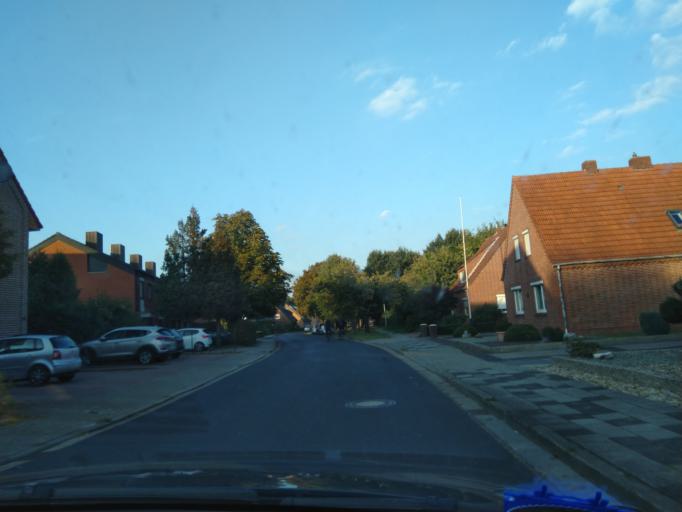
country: DE
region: Lower Saxony
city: Papenburg
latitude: 53.0693
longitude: 7.4352
